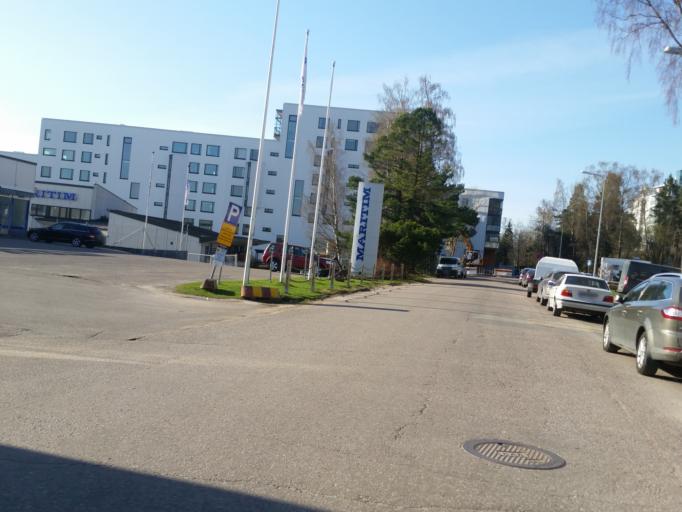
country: FI
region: Uusimaa
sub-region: Helsinki
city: Helsinki
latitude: 60.1499
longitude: 24.8877
